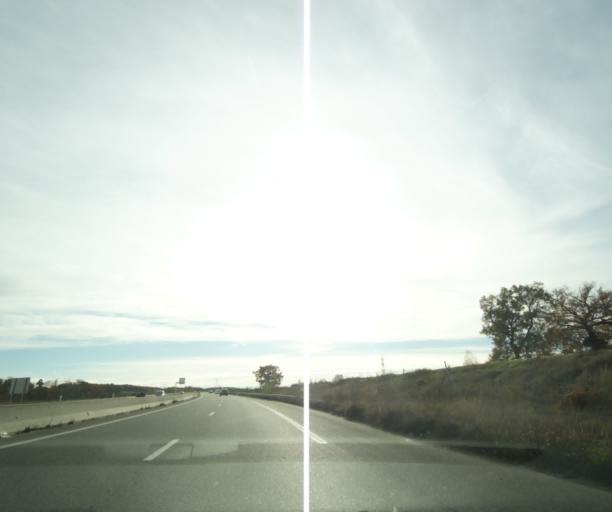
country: FR
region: Midi-Pyrenees
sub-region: Departement de la Haute-Garonne
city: Pibrac
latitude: 43.6002
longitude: 1.2787
